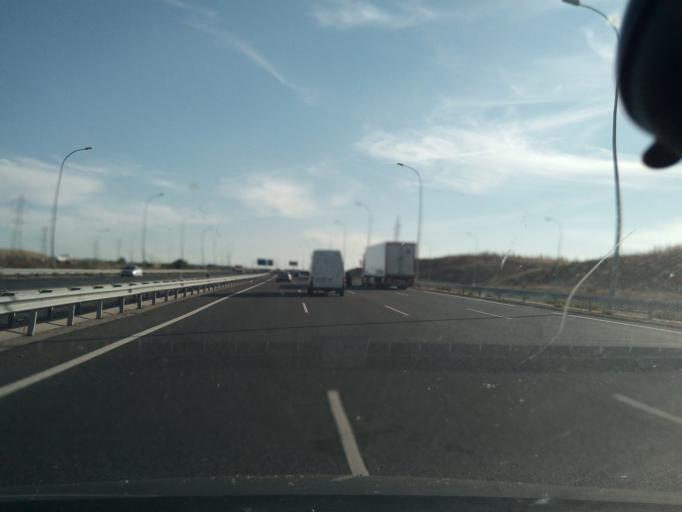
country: ES
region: Madrid
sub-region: Provincia de Madrid
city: Pinto
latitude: 40.2956
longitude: -3.6707
